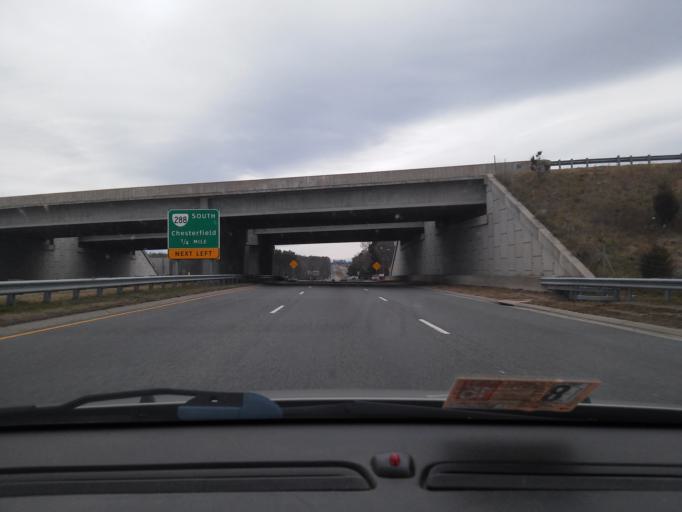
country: US
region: Virginia
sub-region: Henrico County
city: Short Pump
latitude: 37.6641
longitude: -77.6556
